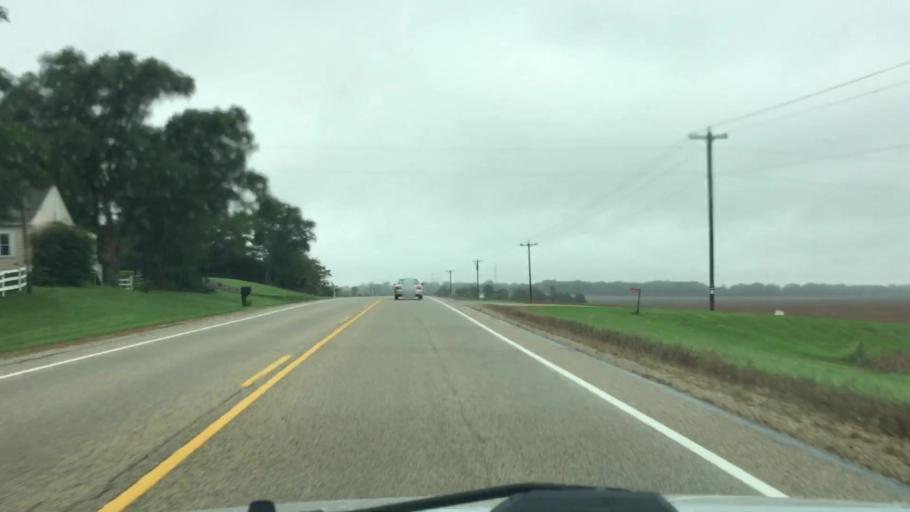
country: US
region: Wisconsin
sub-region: Walworth County
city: Whitewater
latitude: 42.8572
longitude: -88.6770
